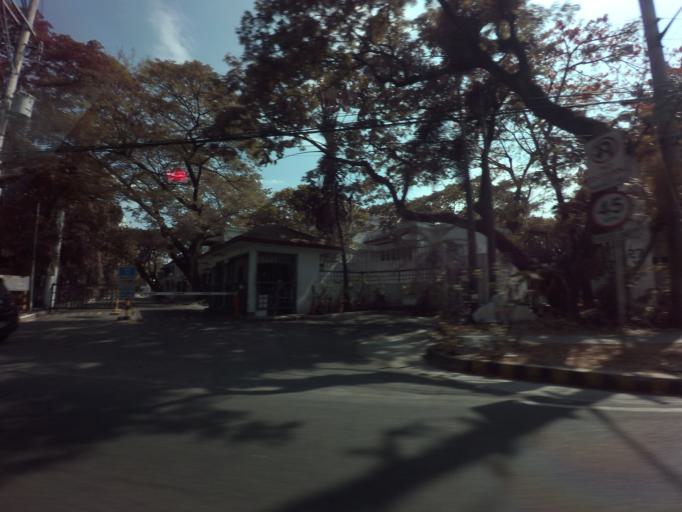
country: PH
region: Metro Manila
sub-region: Makati City
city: Makati City
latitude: 14.5457
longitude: 121.0422
